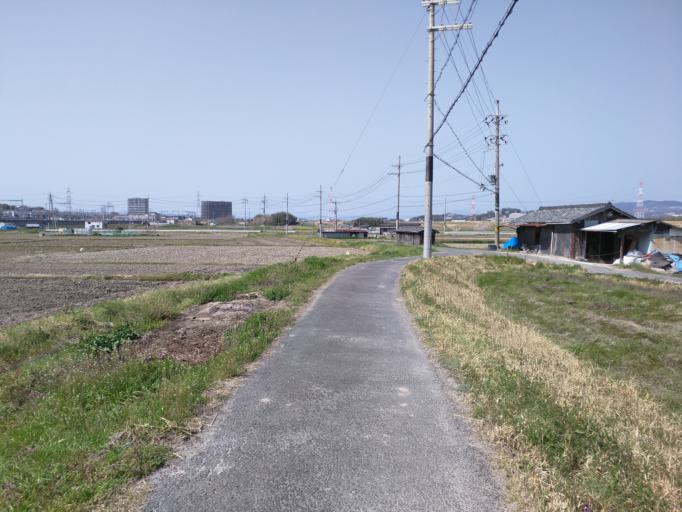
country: JP
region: Kyoto
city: Tanabe
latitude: 34.7886
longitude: 135.7903
